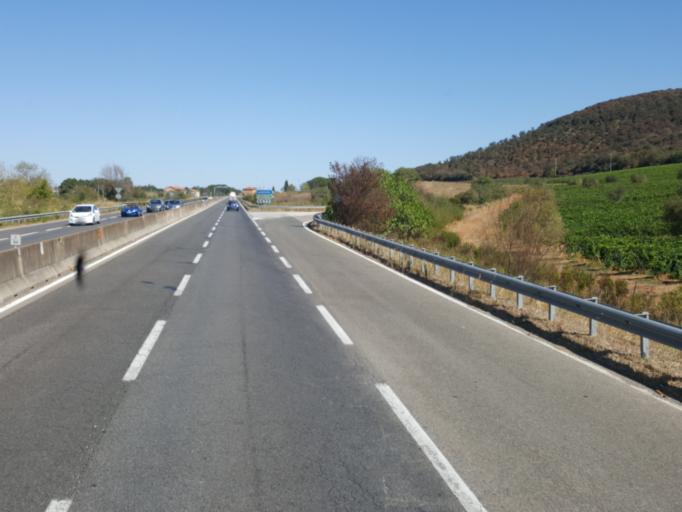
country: IT
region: Tuscany
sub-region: Provincia di Grosseto
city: Fonteblanda
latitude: 42.6323
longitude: 11.1373
